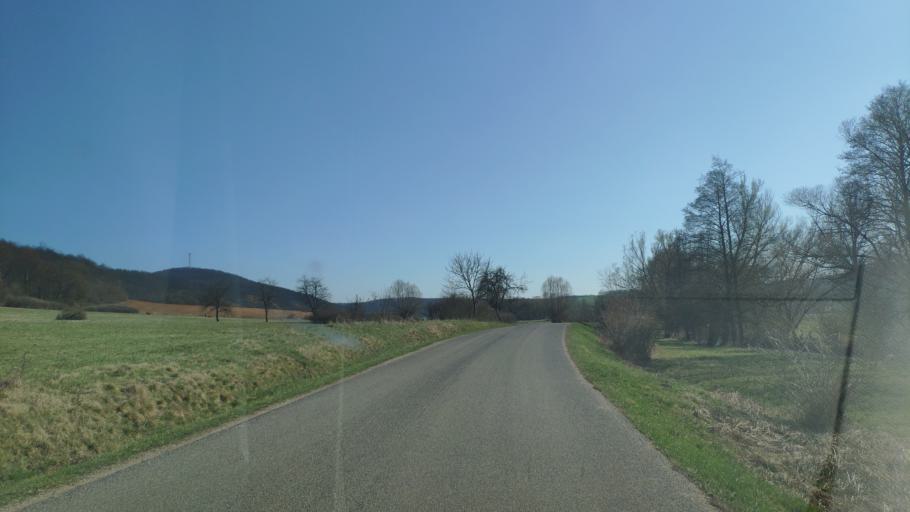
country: SK
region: Banskobystricky
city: Revuca
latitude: 48.5431
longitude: 20.3032
